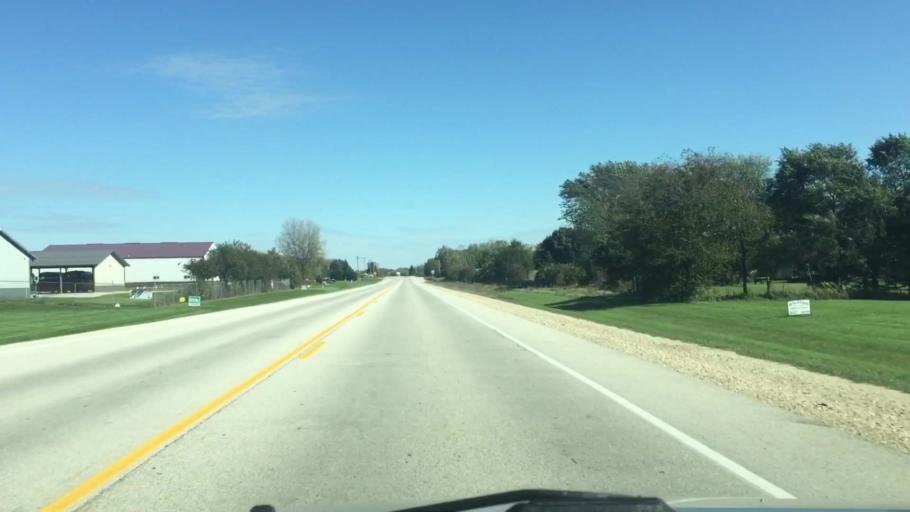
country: US
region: Wisconsin
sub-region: Waukesha County
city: North Prairie
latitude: 42.9372
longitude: -88.3924
